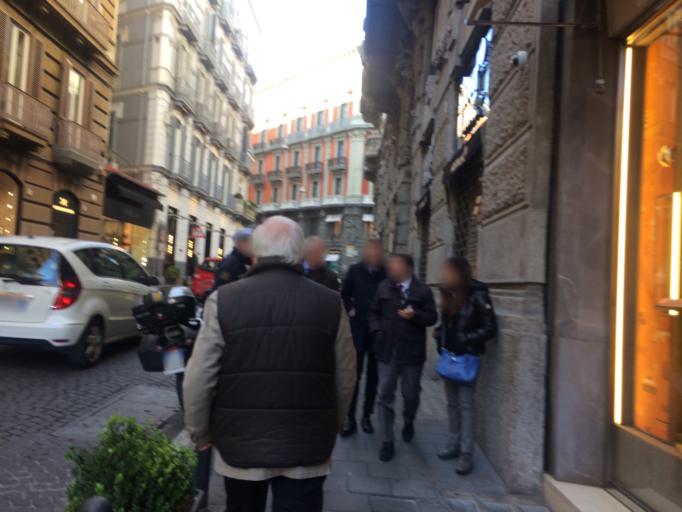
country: IT
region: Campania
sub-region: Provincia di Napoli
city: Napoli
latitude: 40.8362
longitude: 14.2407
